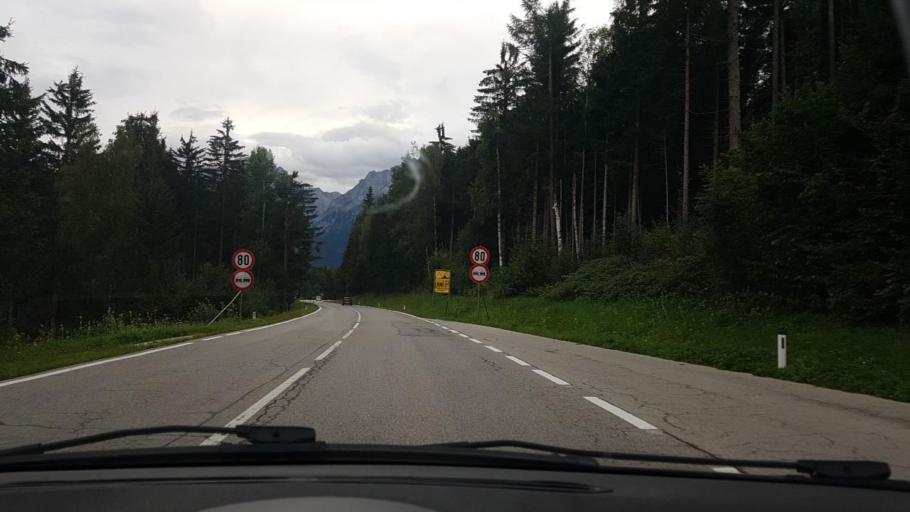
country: AT
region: Tyrol
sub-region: Politischer Bezirk Lienz
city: Dolsach
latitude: 46.8473
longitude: 12.8525
